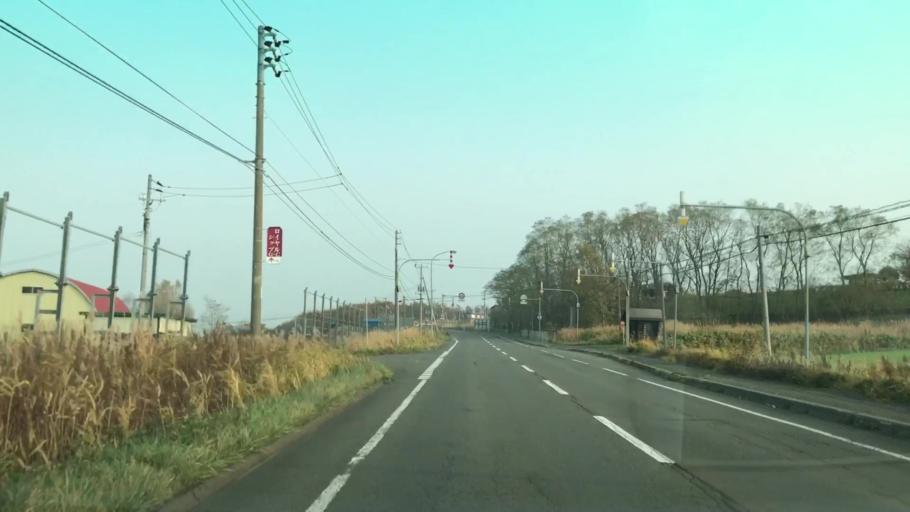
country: JP
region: Hokkaido
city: Ishikari
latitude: 43.2735
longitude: 141.4028
